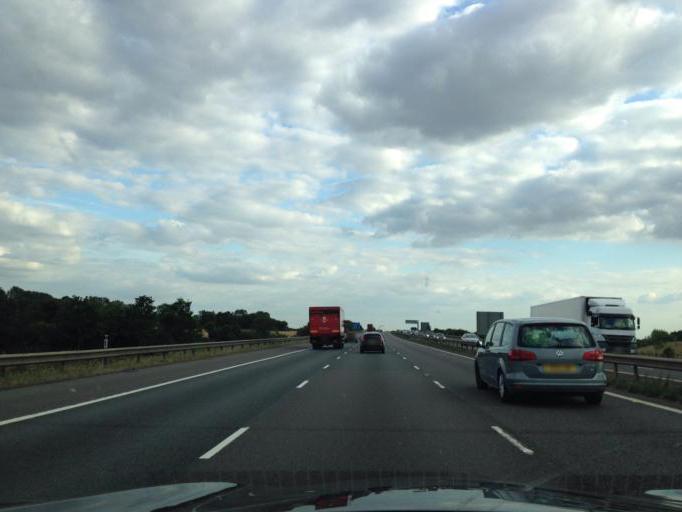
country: GB
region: England
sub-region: Oxfordshire
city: Bicester
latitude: 51.9341
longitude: -1.2017
